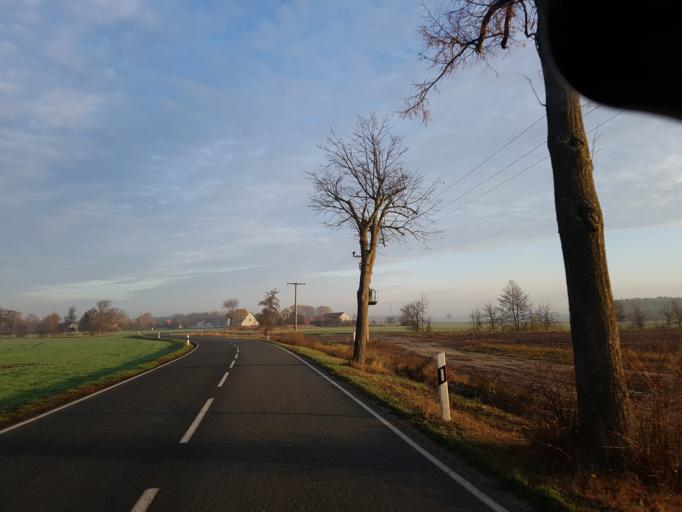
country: DE
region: Saxony-Anhalt
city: Elster
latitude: 51.8432
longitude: 12.8373
